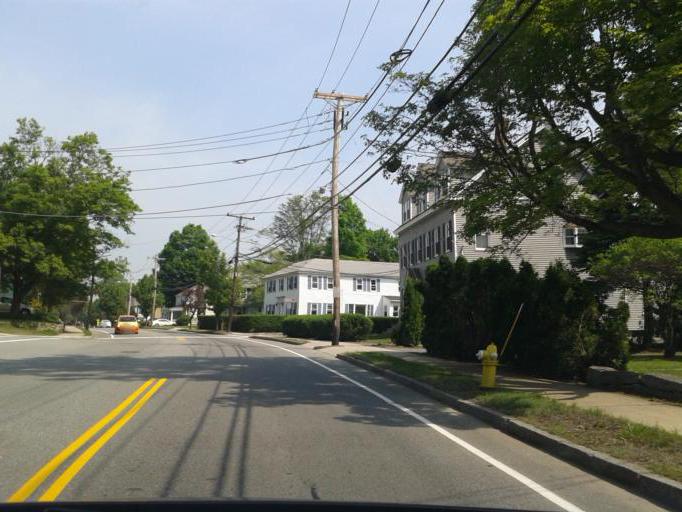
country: US
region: Massachusetts
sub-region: Worcester County
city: Westborough
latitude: 42.2645
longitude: -71.6100
